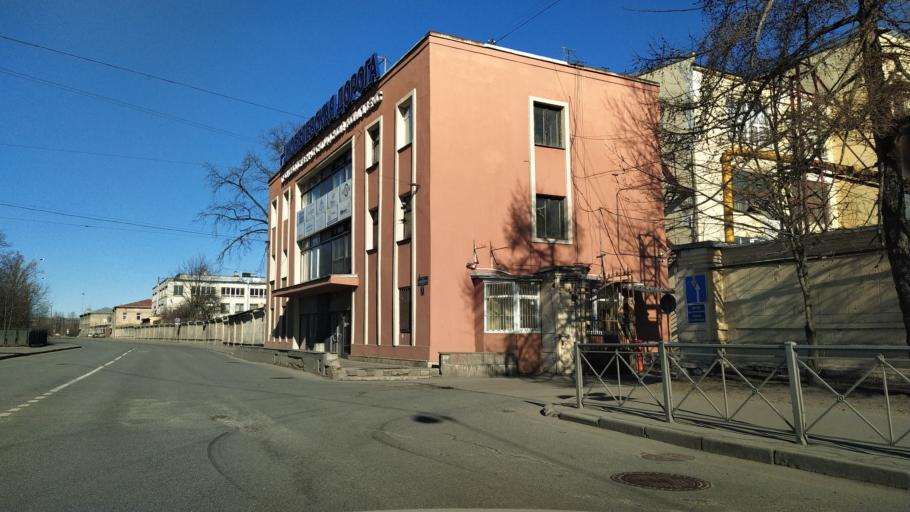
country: RU
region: St.-Petersburg
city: Centralniy
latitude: 59.9005
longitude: 30.3728
